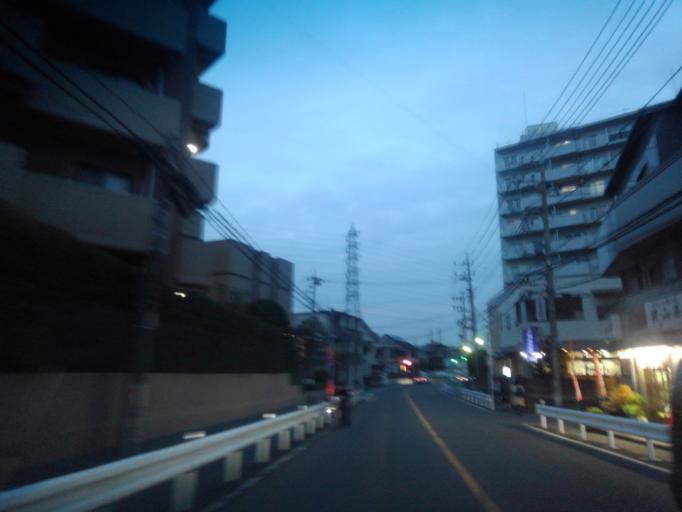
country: JP
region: Saitama
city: Tokorozawa
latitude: 35.8082
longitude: 139.4516
